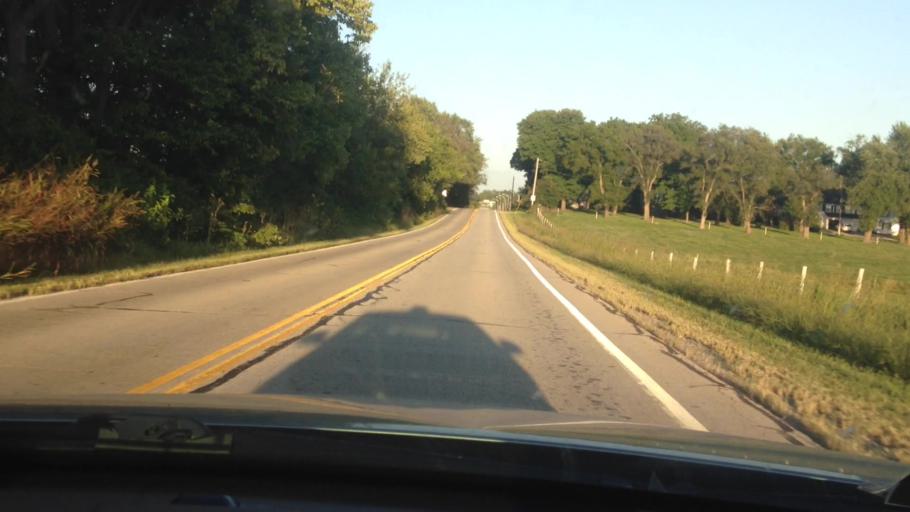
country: US
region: Missouri
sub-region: Clay County
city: Smithville
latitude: 39.3039
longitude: -94.5969
